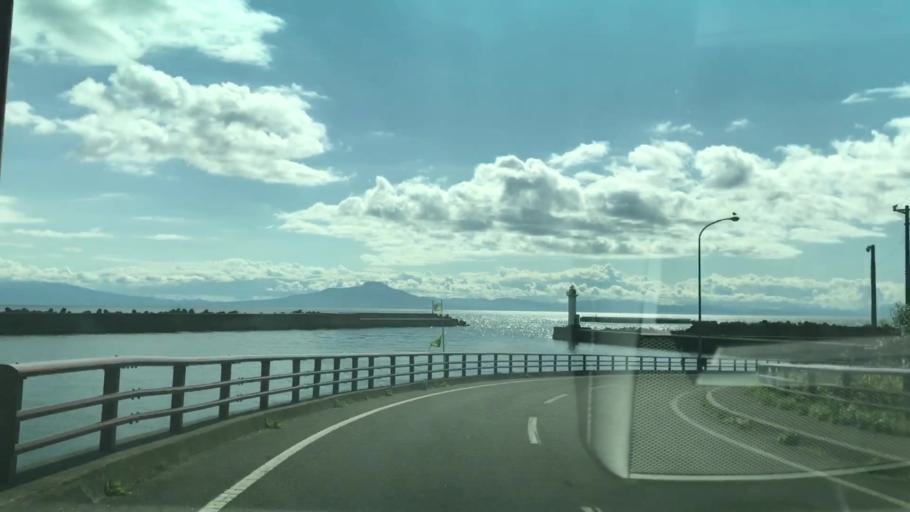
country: JP
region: Hokkaido
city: Muroran
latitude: 42.3076
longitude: 140.9696
